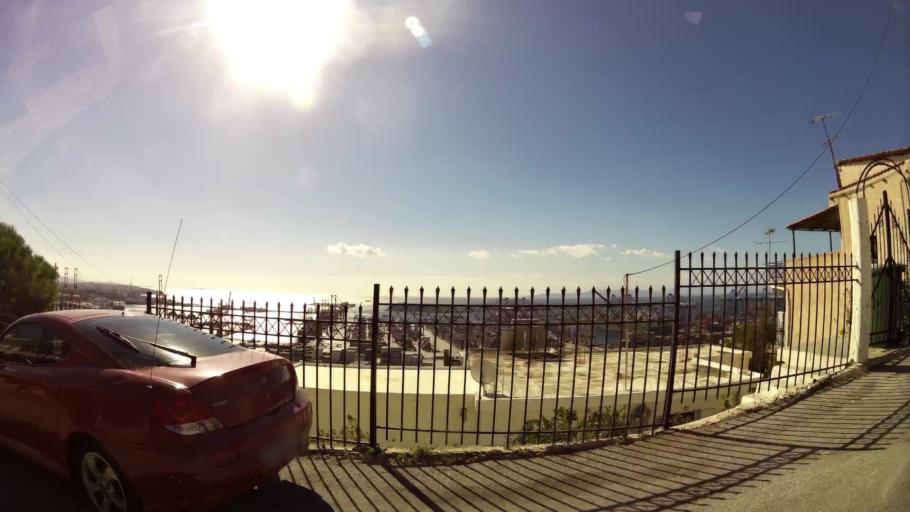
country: GR
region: Attica
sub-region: Nomos Piraios
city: Perama
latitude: 37.9651
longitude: 23.5905
